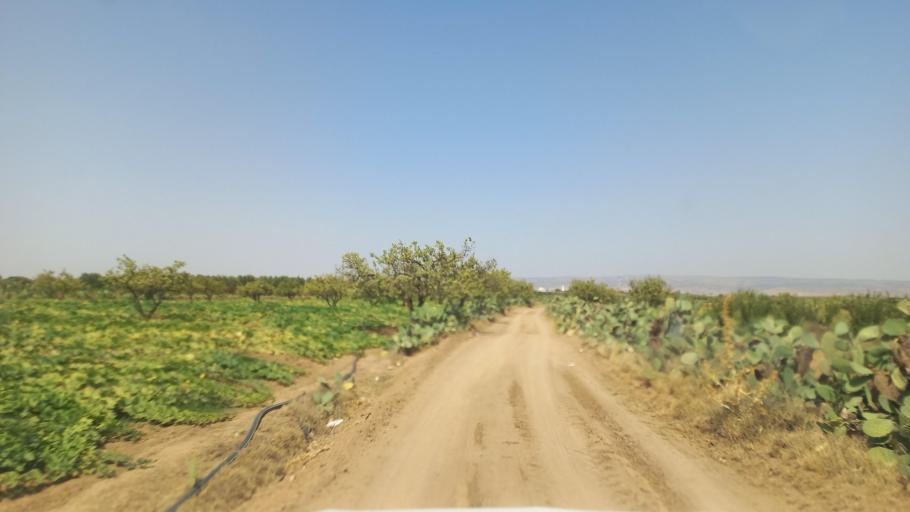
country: TN
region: Al Qasrayn
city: Kasserine
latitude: 35.2459
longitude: 9.0402
